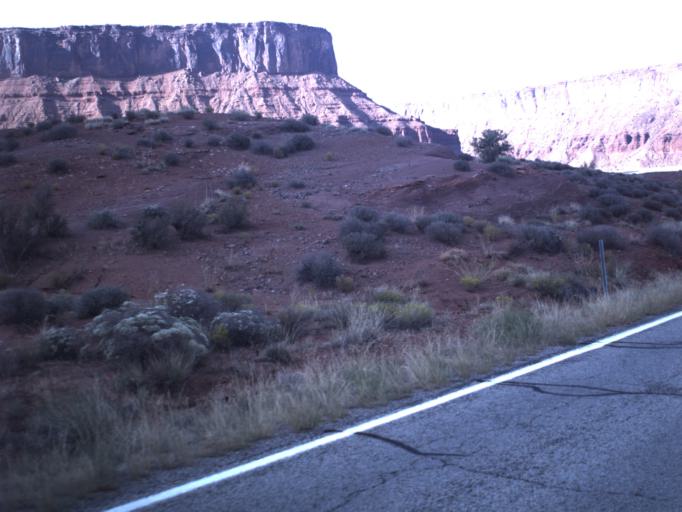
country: US
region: Utah
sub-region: Grand County
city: Moab
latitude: 38.7408
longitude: -109.3326
